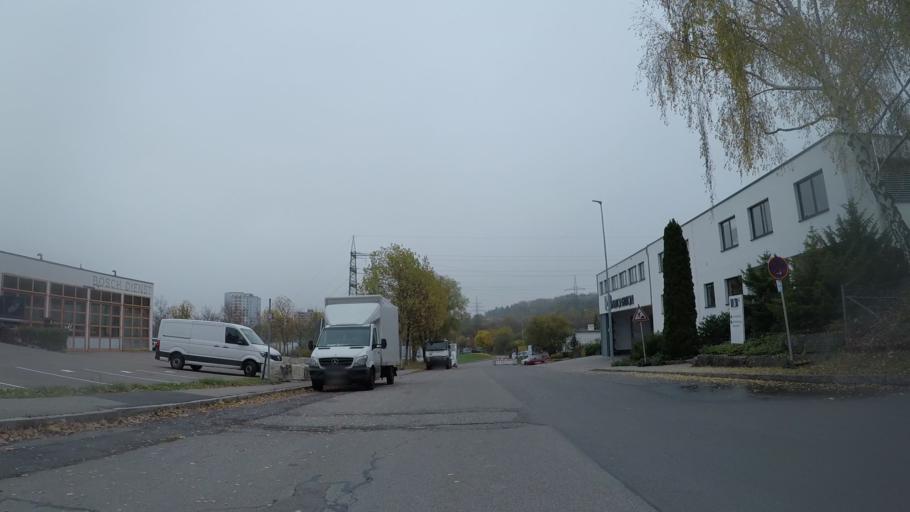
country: DE
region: Baden-Wuerttemberg
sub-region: Tuebingen Region
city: Reutlingen
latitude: 48.5081
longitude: 9.2301
